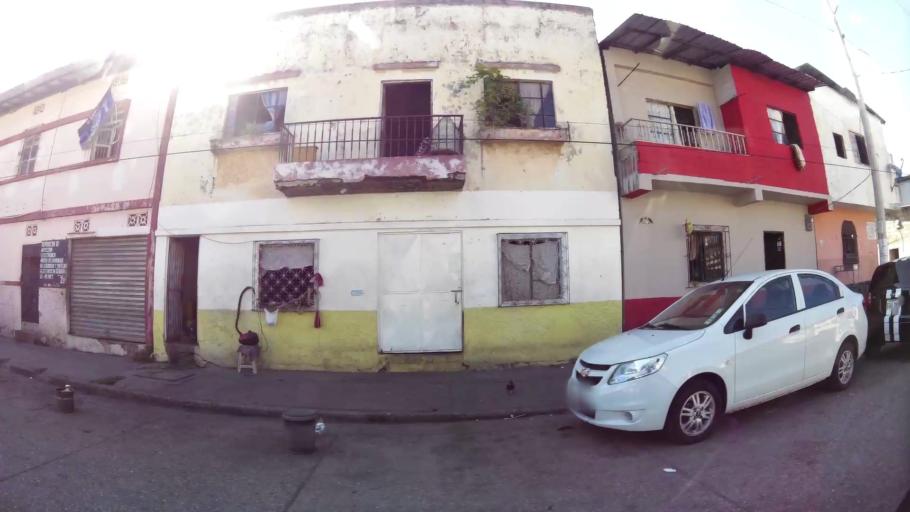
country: EC
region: Guayas
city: Guayaquil
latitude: -2.1756
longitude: -79.8949
